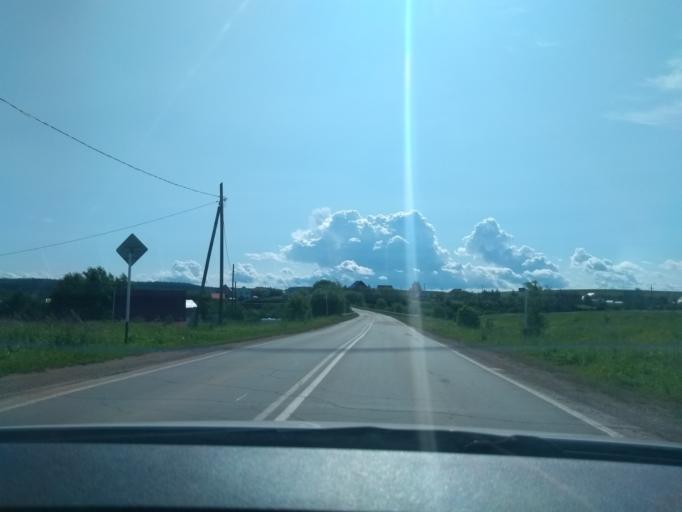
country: RU
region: Perm
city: Lobanovo
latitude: 57.8505
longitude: 56.3381
